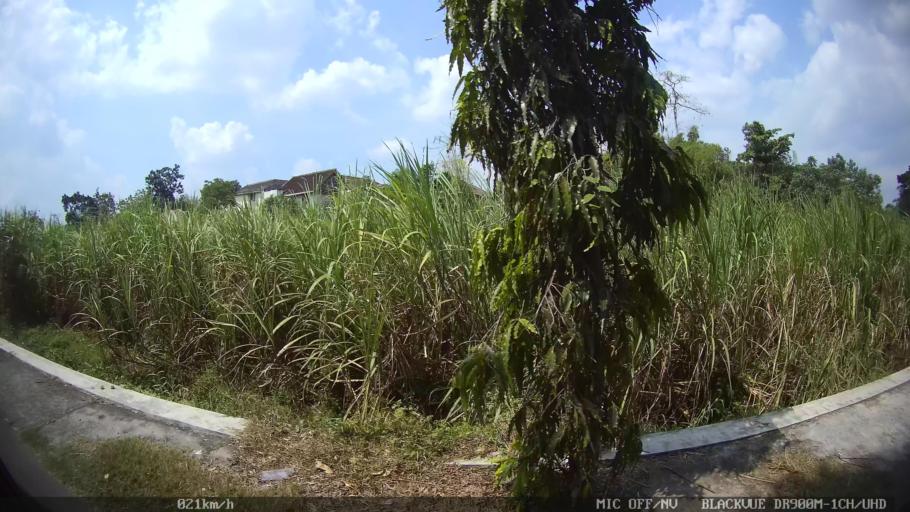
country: ID
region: Daerah Istimewa Yogyakarta
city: Yogyakarta
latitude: -7.8090
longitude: 110.4062
